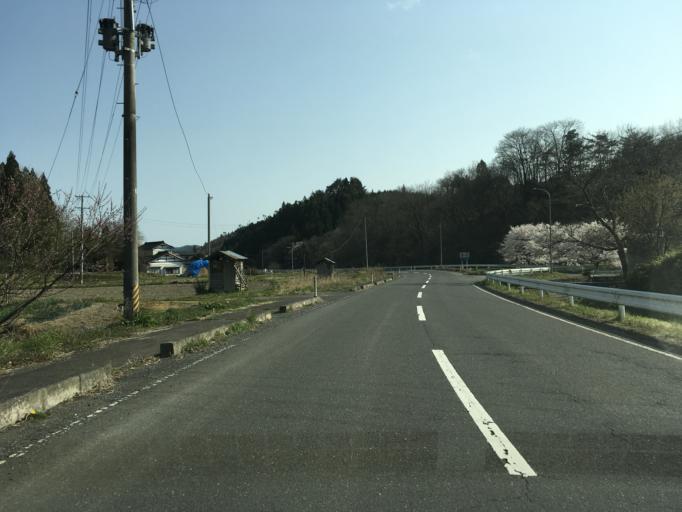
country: JP
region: Iwate
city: Ichinoseki
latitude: 38.8015
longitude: 141.3178
